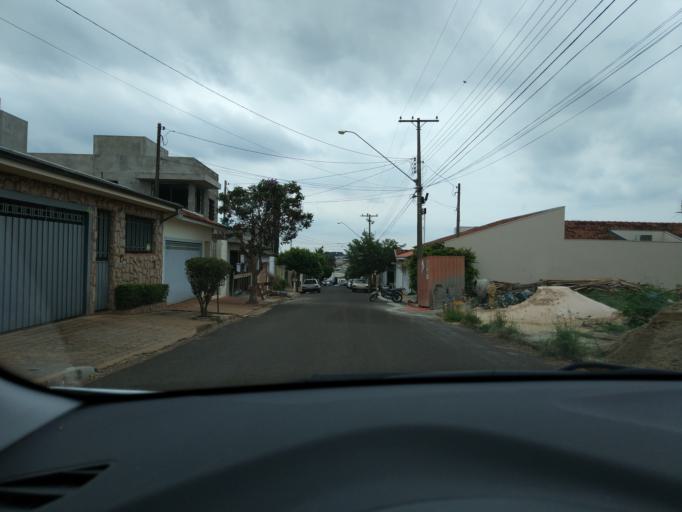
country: BR
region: Sao Paulo
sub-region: Jau
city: Jau
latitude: -22.2821
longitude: -48.5421
